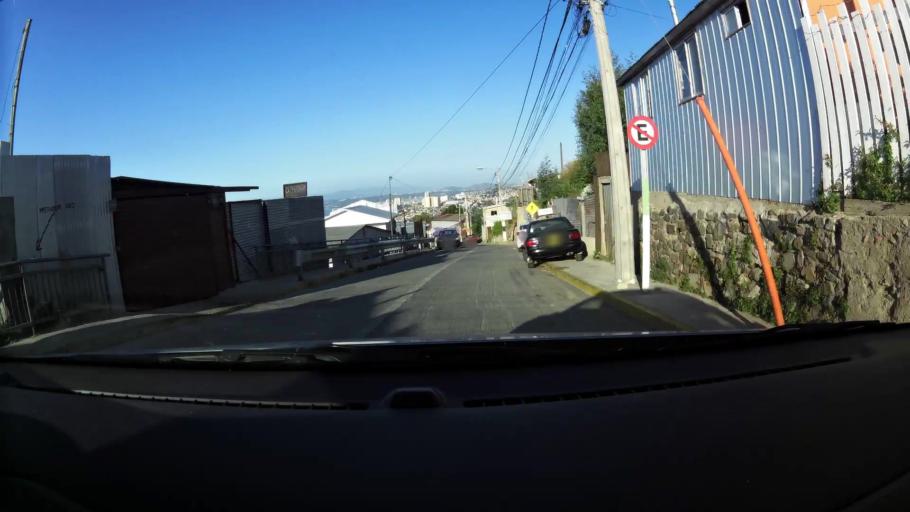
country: CL
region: Valparaiso
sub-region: Provincia de Valparaiso
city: Valparaiso
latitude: -33.0578
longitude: -71.6158
